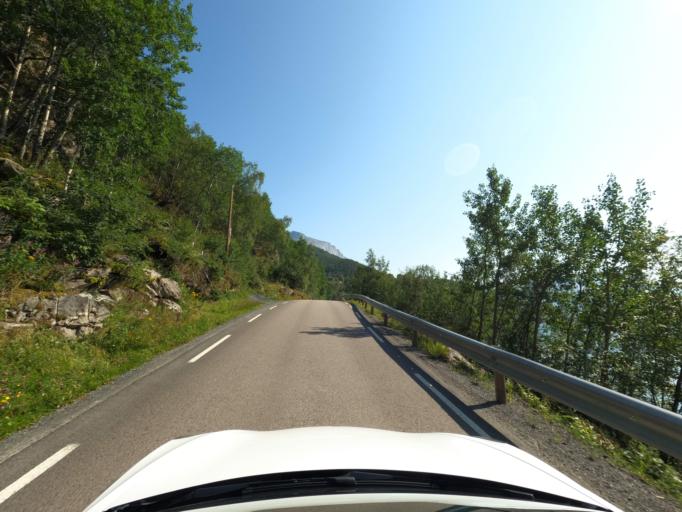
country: NO
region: Nordland
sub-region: Narvik
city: Narvik
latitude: 68.2975
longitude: 17.3520
